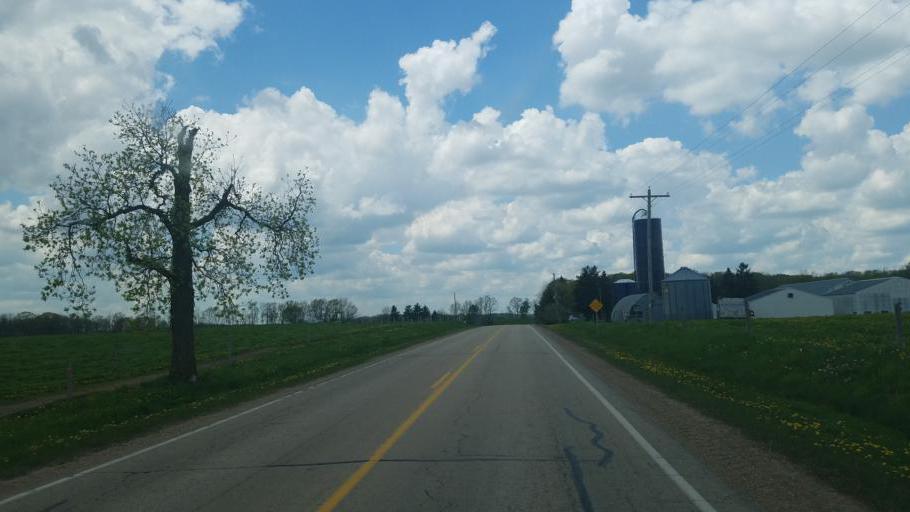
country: US
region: Wisconsin
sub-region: Vernon County
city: Hillsboro
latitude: 43.5937
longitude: -90.3056
